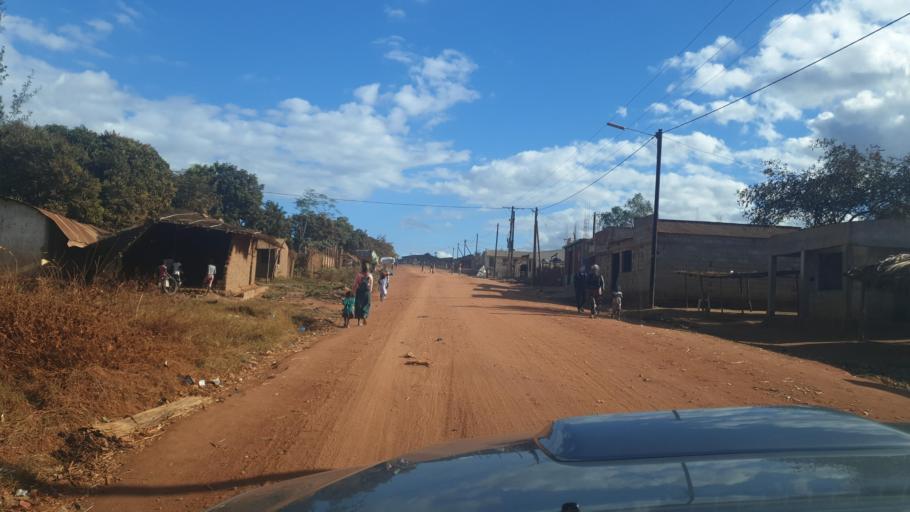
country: MZ
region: Nampula
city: Nampula
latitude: -15.1002
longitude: 39.2225
